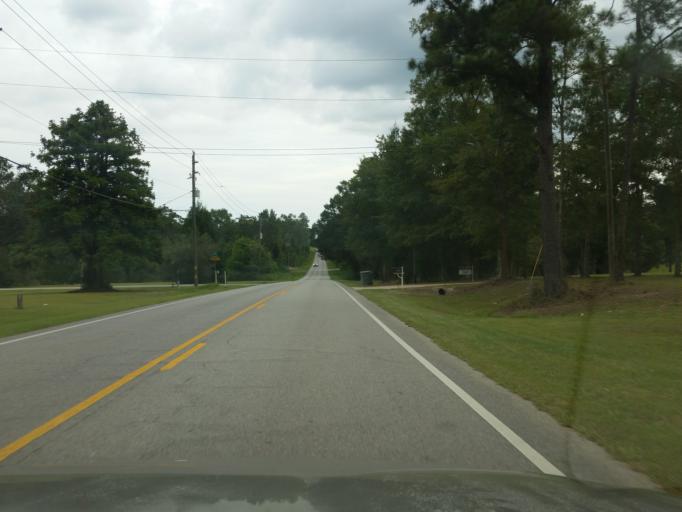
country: US
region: Florida
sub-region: Escambia County
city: Molino
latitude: 30.7104
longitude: -87.3357
